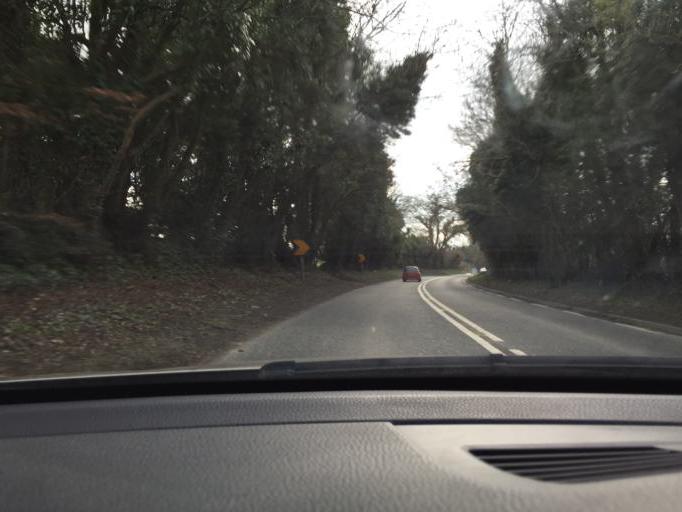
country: IE
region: Leinster
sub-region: Wicklow
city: Blessington
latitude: 53.1608
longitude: -6.5485
